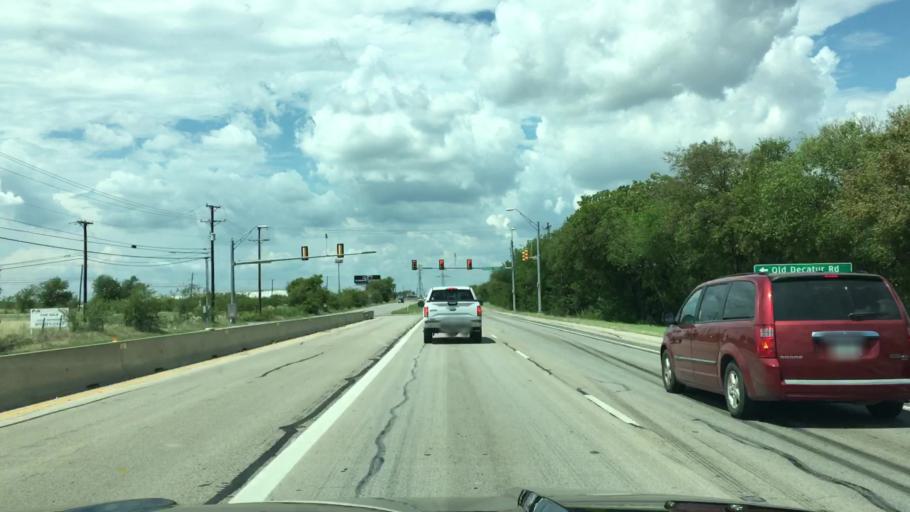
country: US
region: Texas
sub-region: Tarrant County
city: Eagle Mountain
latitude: 32.8988
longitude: -97.3973
